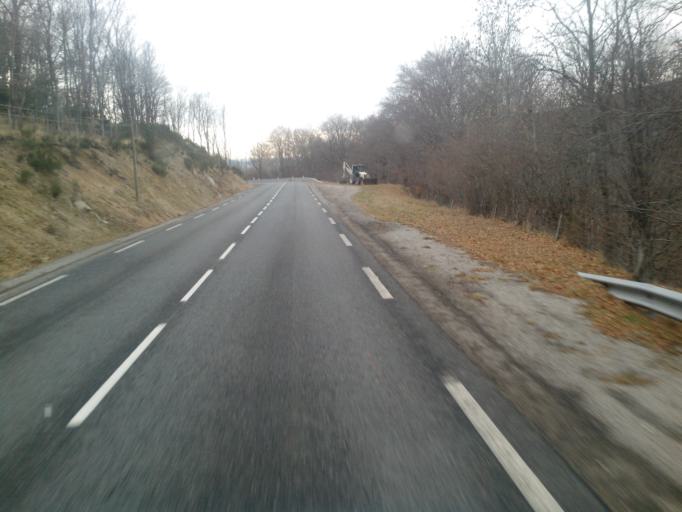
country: FR
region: Languedoc-Roussillon
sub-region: Departement de la Lozere
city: Mende
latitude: 44.5827
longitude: 3.4956
